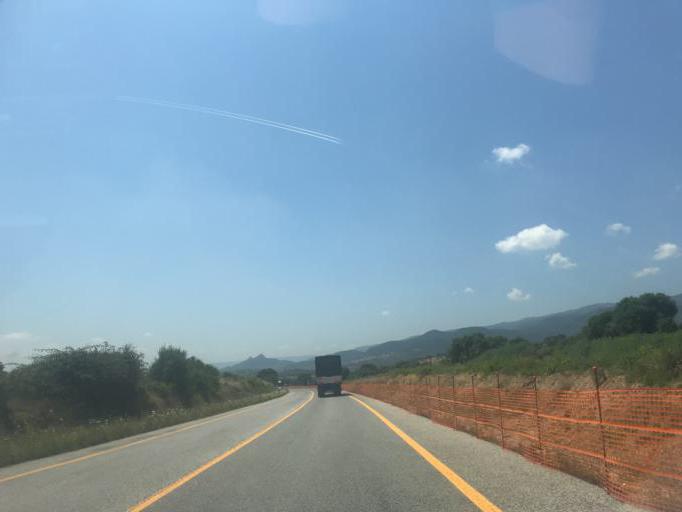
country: IT
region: Sardinia
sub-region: Provincia di Olbia-Tempio
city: Berchidda
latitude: 40.7813
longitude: 9.2199
